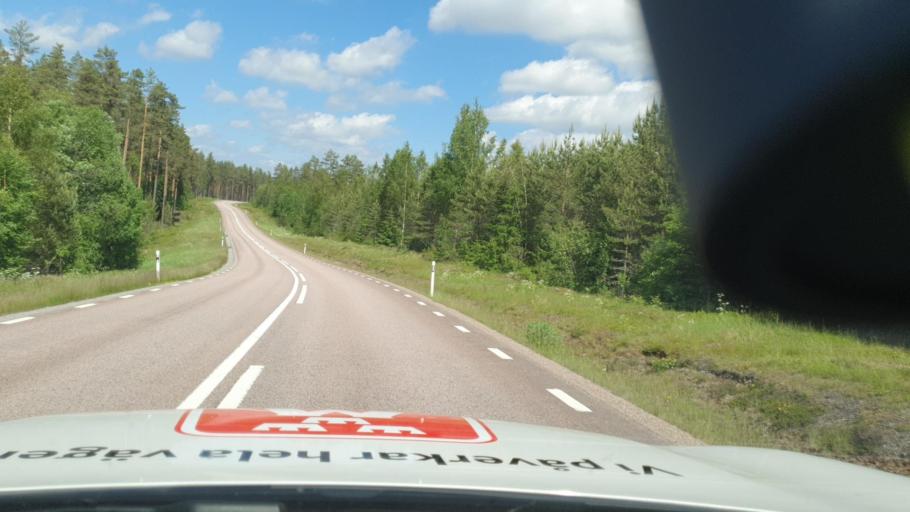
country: SE
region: Vaermland
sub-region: Filipstads Kommun
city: Filipstad
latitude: 59.6285
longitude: 13.9526
